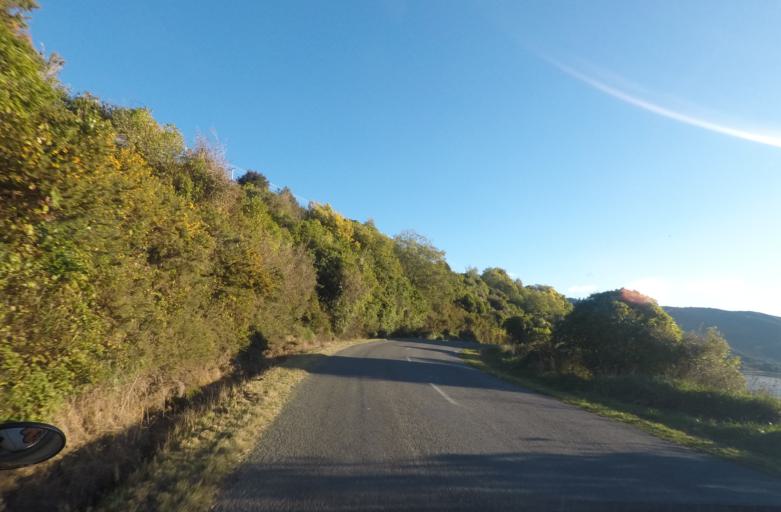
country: NZ
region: Marlborough
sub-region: Marlborough District
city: Picton
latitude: -41.2925
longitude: 173.8408
